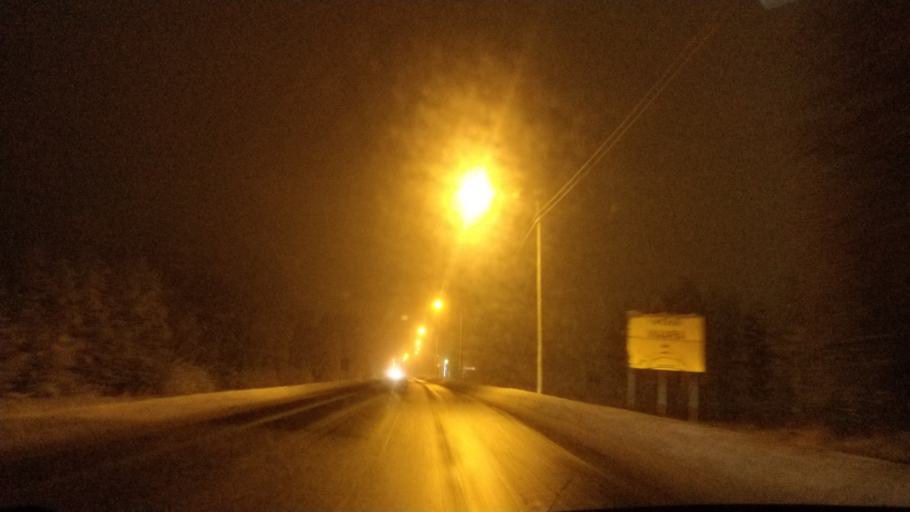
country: FI
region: Lapland
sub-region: Rovaniemi
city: Rovaniemi
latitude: 66.4804
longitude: 25.6280
